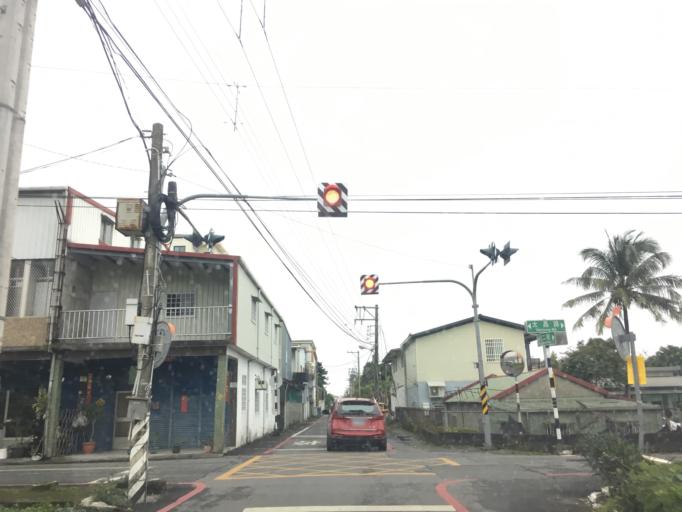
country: TW
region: Taiwan
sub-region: Hualien
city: Hualian
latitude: 23.9896
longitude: 121.5705
